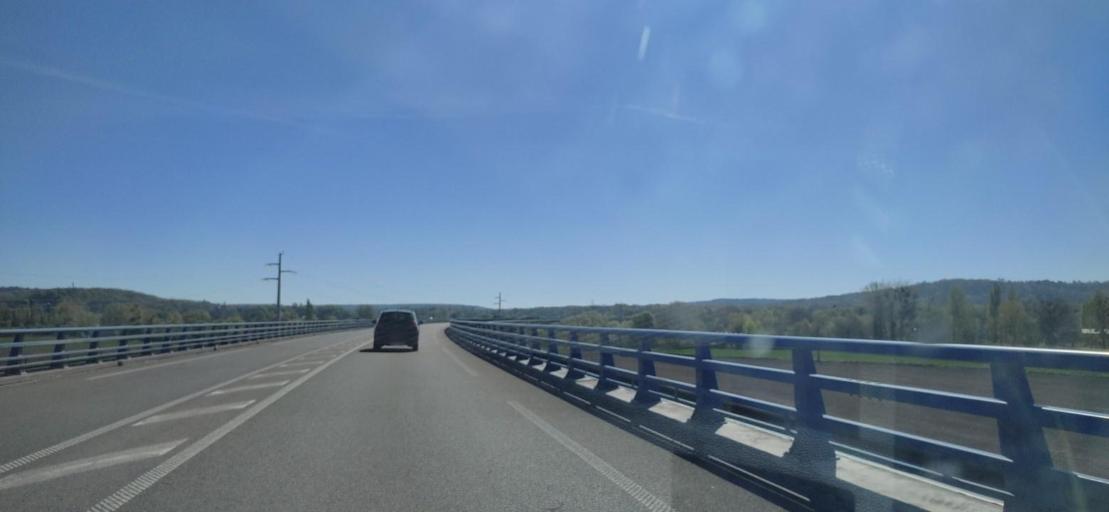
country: FR
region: Picardie
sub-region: Departement de l'Oise
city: Clairoix
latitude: 49.4352
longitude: 2.8594
